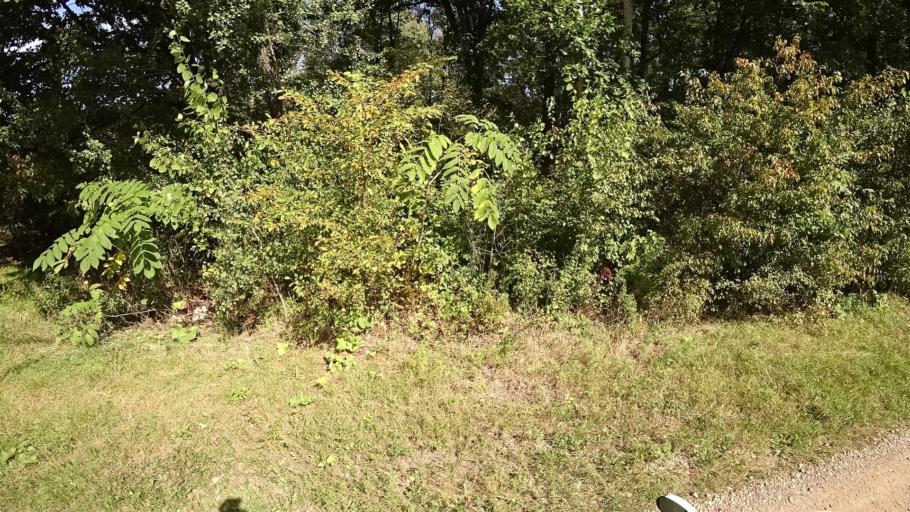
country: RU
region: Primorskiy
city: Kirovskiy
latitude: 44.7606
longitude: 133.6196
